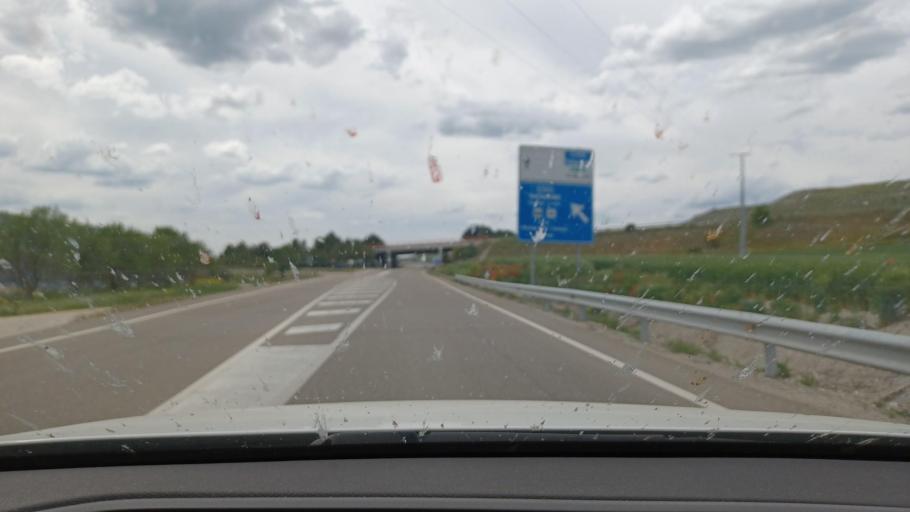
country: ES
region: Castille and Leon
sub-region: Provincia de Segovia
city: Cuellar
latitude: 41.3878
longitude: -4.2905
